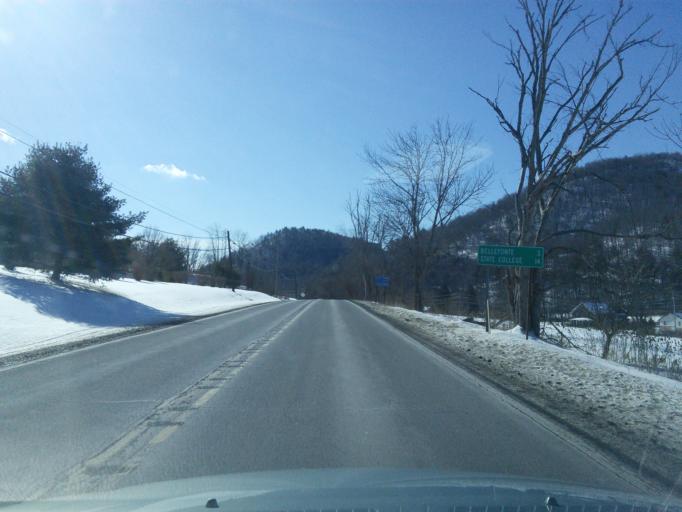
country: US
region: Pennsylvania
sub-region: Centre County
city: Milesburg
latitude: 40.9353
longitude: -77.7853
